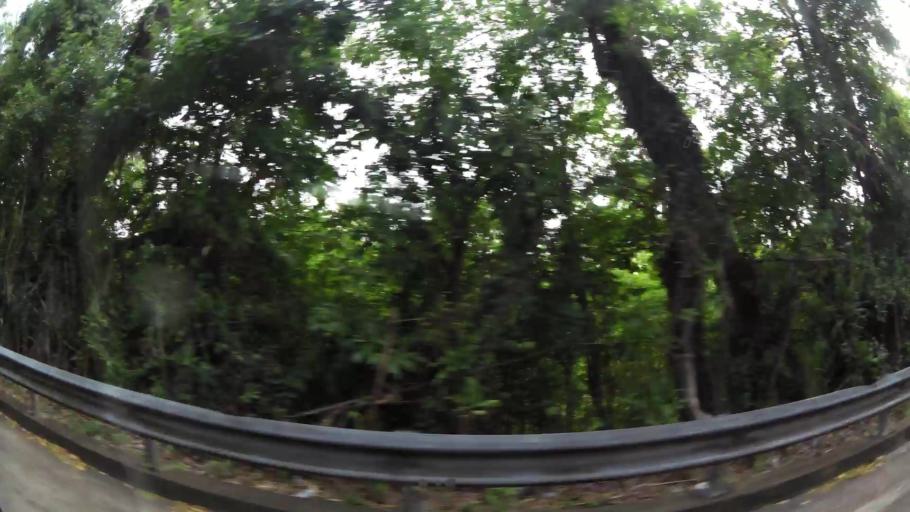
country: GP
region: Guadeloupe
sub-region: Guadeloupe
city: Basse-Terre
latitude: 16.0071
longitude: -61.7119
